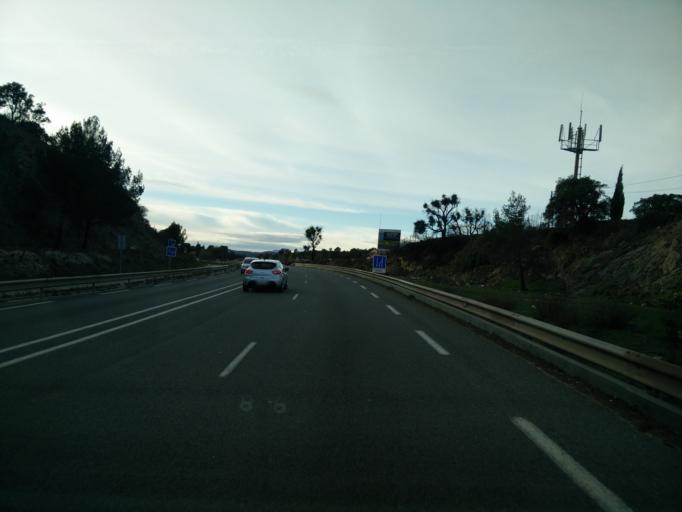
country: FR
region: Provence-Alpes-Cote d'Azur
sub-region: Departement du Var
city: Bormes-les-Mimosas
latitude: 43.1507
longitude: 6.2876
